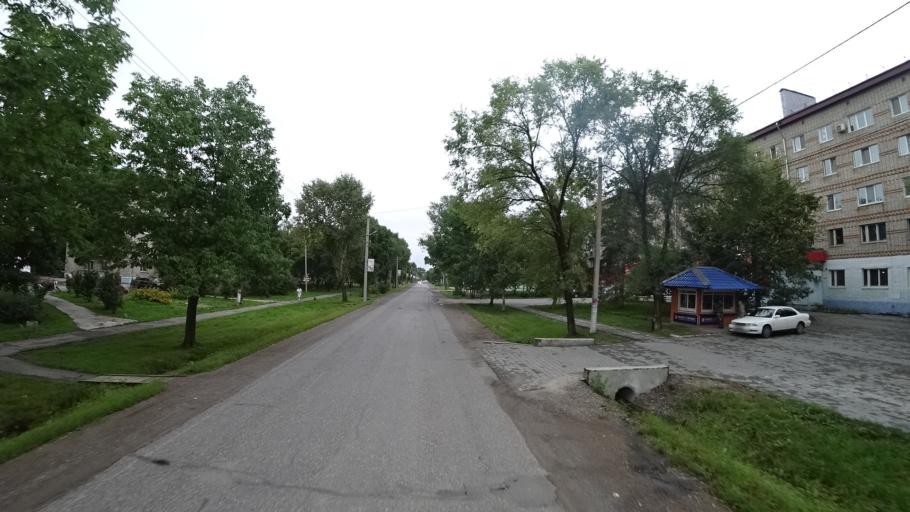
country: RU
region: Primorskiy
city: Chernigovka
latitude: 44.3427
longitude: 132.5761
